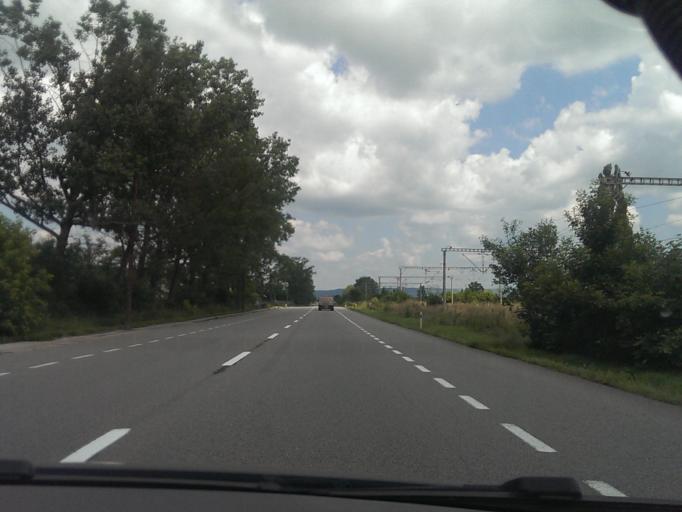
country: RO
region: Cluj
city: Jucu Herghelia
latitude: 46.8639
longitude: 23.7640
